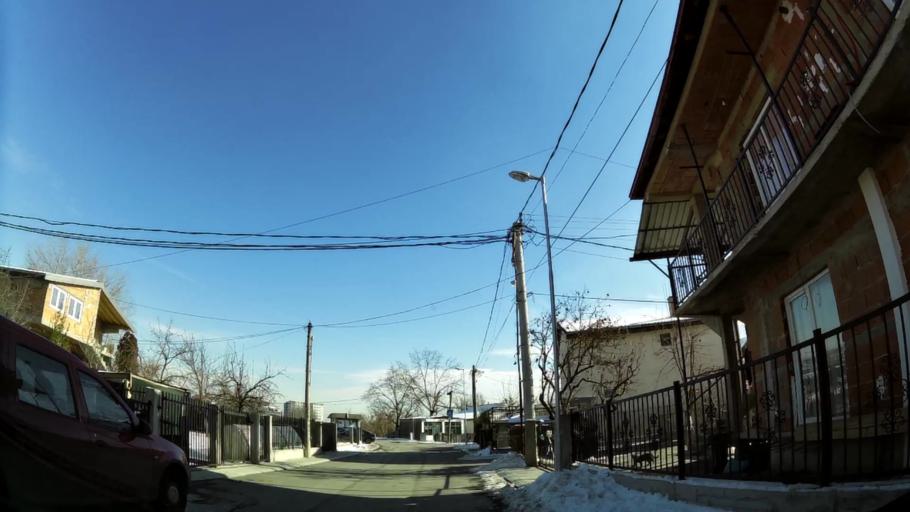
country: MK
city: Krushopek
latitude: 42.0021
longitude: 21.3563
